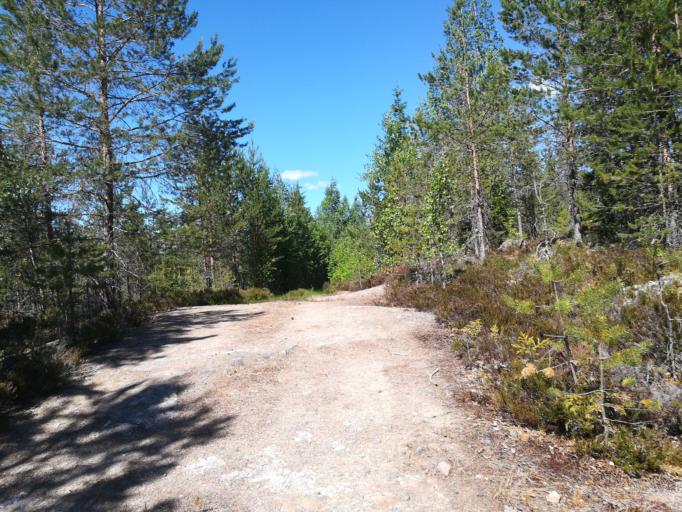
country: FI
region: Southern Savonia
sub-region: Mikkeli
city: Puumala
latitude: 61.6182
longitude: 28.1619
